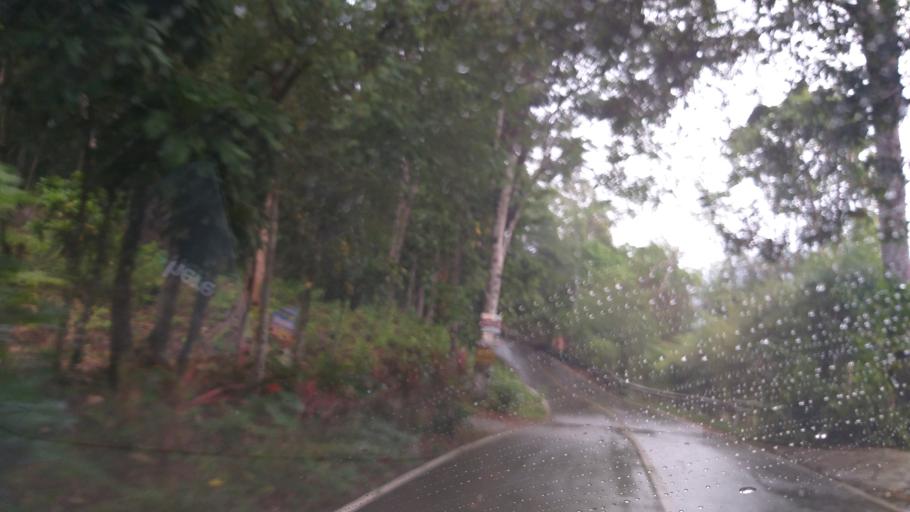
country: TH
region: Trat
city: Ko Chang Tai
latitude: 11.9756
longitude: 102.3222
